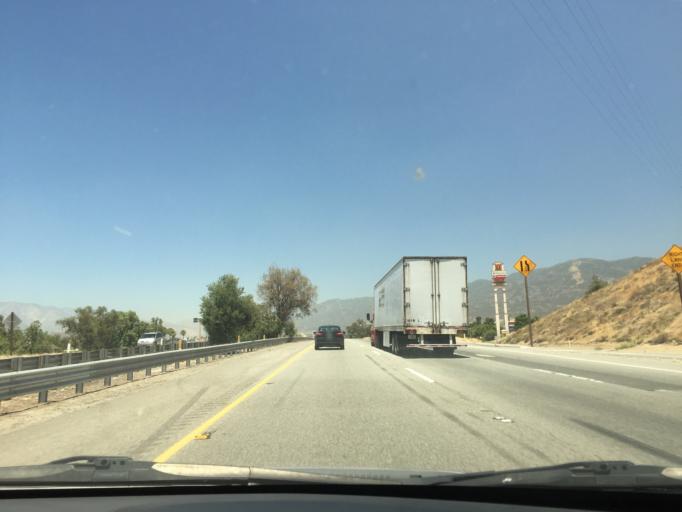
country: US
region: California
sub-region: San Bernardino County
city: Muscoy
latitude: 34.1621
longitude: -117.3312
